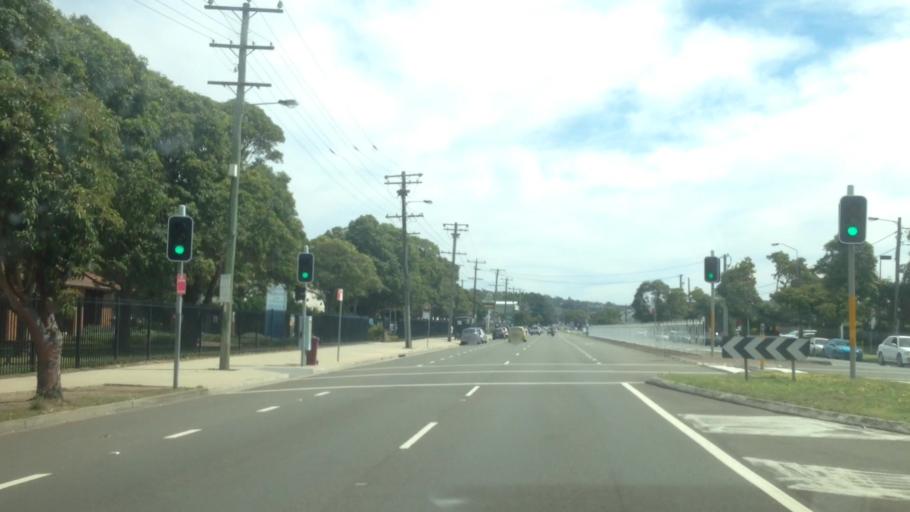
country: AU
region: New South Wales
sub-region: Newcastle
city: Broadmeadow
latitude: -32.9238
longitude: 151.7283
